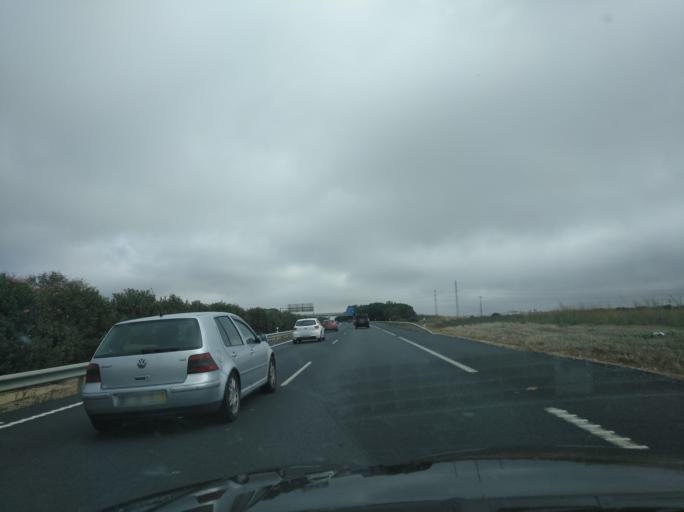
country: ES
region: Andalusia
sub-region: Provincia de Huelva
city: San Juan del Puerto
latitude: 37.3175
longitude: -6.8587
